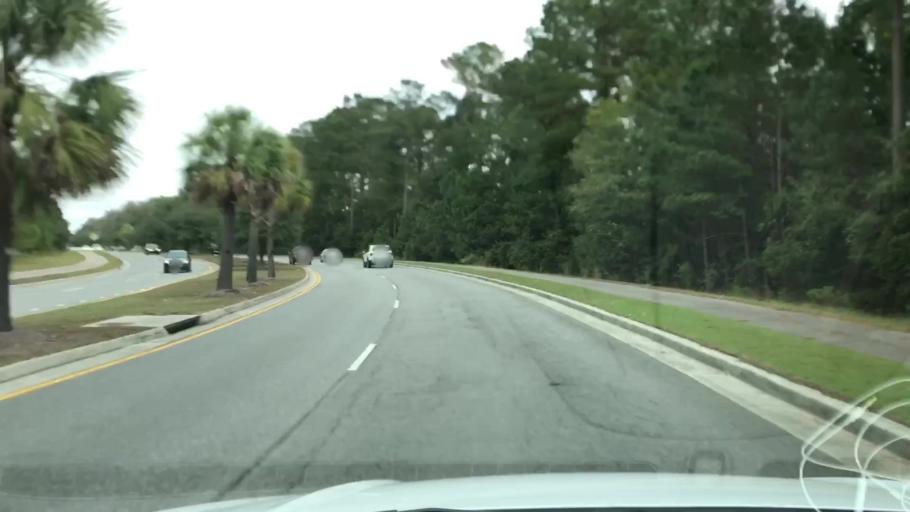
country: US
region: South Carolina
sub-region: Beaufort County
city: Bluffton
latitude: 32.2571
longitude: -80.8922
